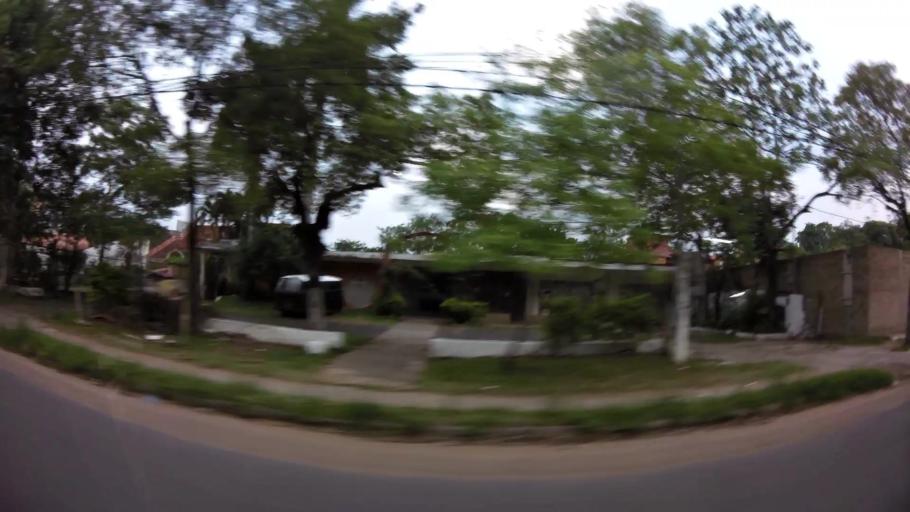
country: PY
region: Central
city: Lambare
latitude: -25.3388
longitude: -57.6347
